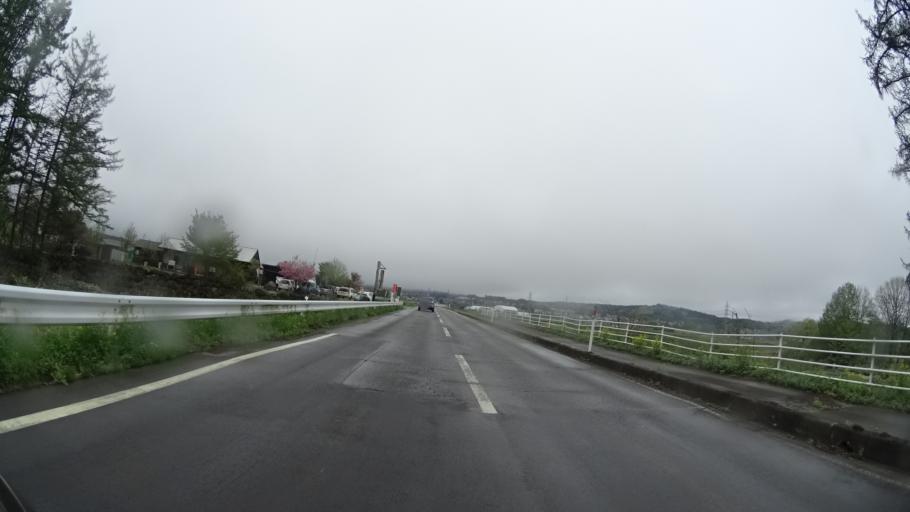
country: JP
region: Nagano
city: Nagano-shi
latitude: 36.7945
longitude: 138.1957
